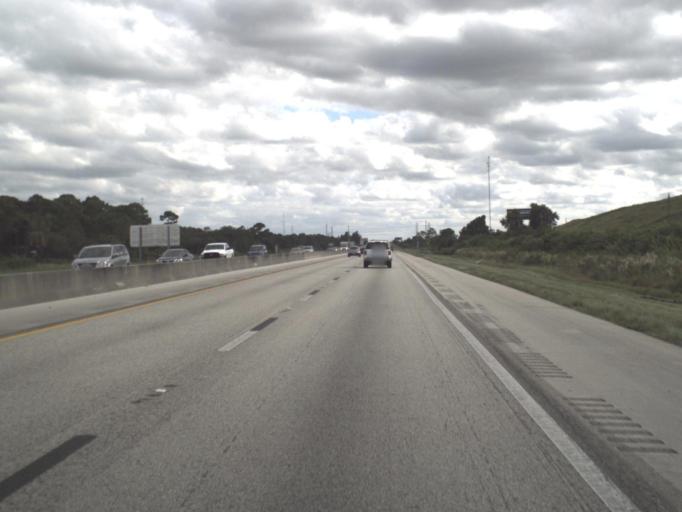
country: US
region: Florida
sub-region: Saint Lucie County
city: Fort Pierce South
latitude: 27.3914
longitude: -80.3924
